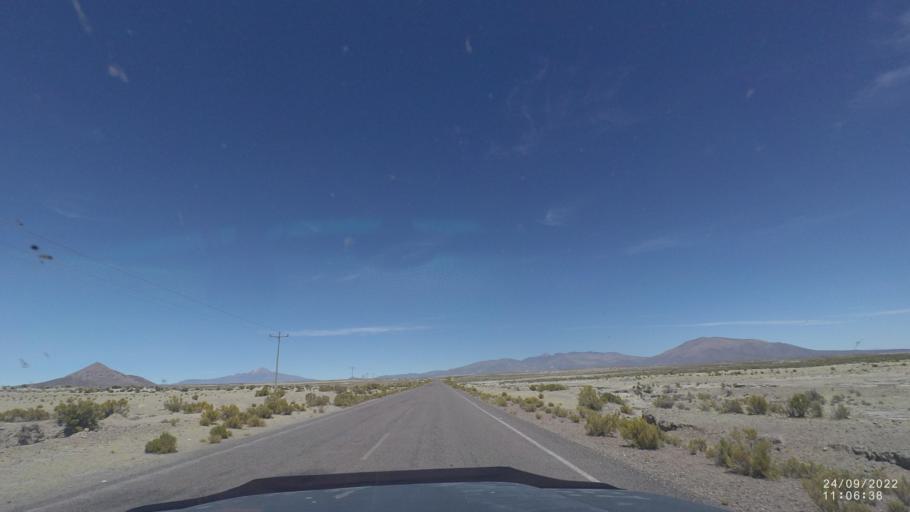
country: BO
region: Oruro
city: Challapata
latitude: -19.4772
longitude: -67.4317
